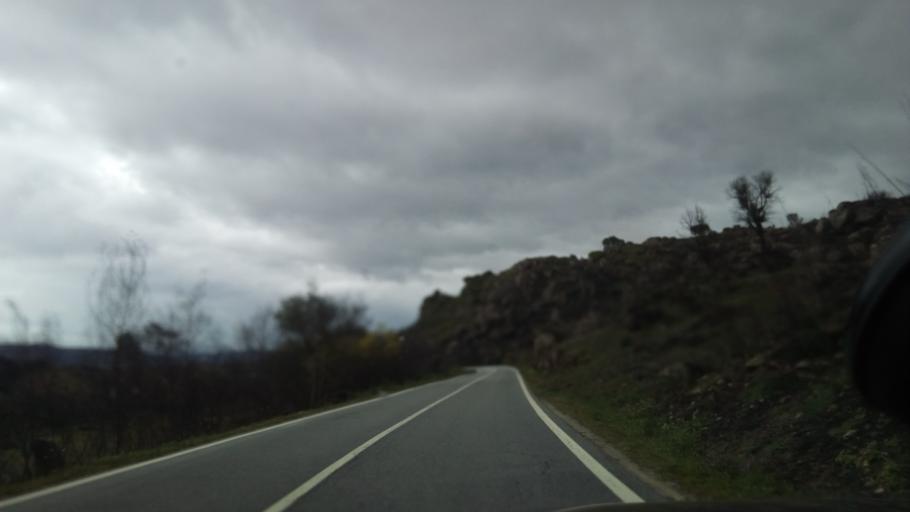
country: PT
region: Guarda
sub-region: Fornos de Algodres
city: Fornos de Algodres
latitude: 40.5622
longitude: -7.5594
